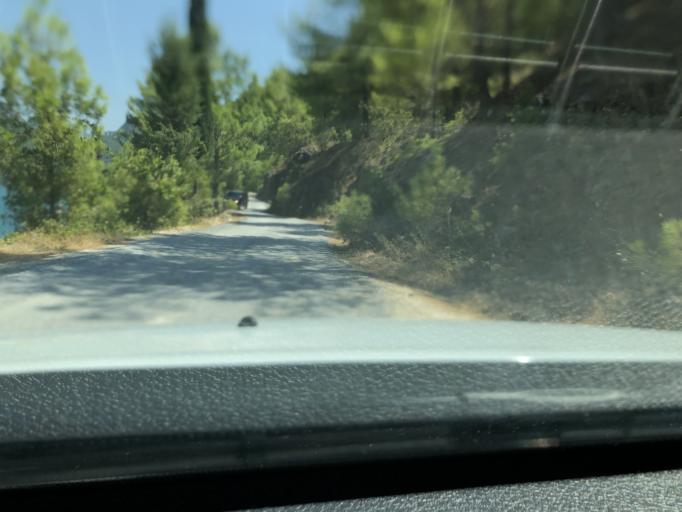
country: TR
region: Antalya
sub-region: Manavgat
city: Manavgat
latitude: 36.9079
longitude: 31.5545
